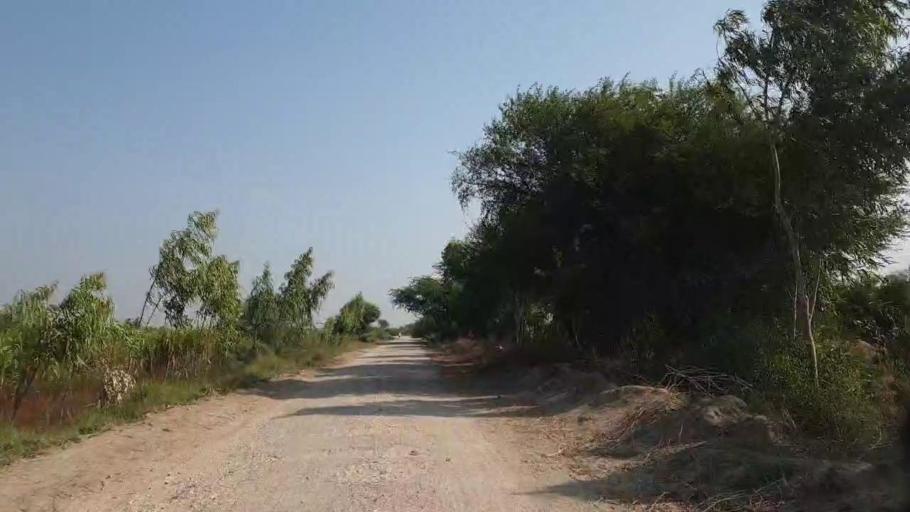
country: PK
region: Sindh
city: Bulri
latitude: 24.9312
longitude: 68.3746
